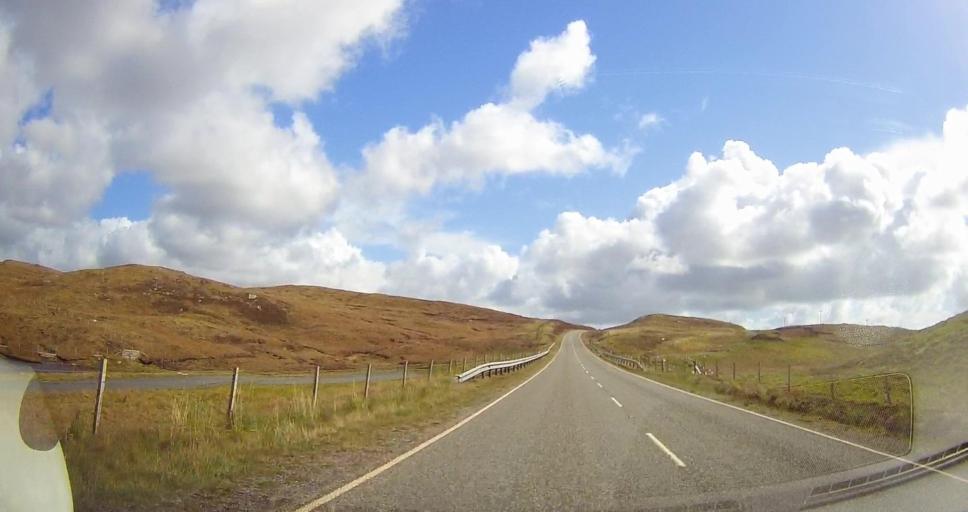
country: GB
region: Scotland
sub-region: Shetland Islands
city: Lerwick
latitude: 60.4747
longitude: -1.4077
